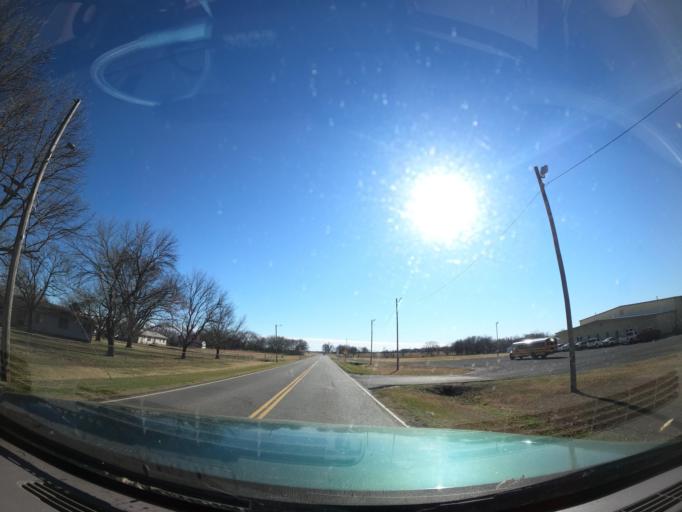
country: US
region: Oklahoma
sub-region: McIntosh County
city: Checotah
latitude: 35.5533
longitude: -95.6515
